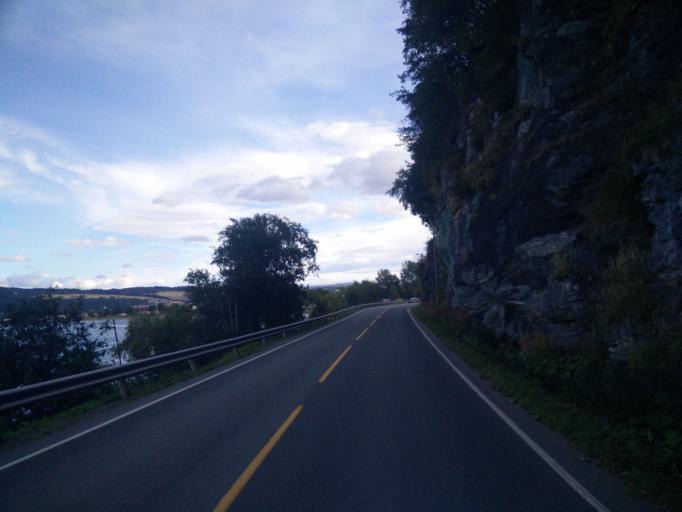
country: NO
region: Sor-Trondelag
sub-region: Melhus
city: Melhus
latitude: 63.3223
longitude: 10.2053
